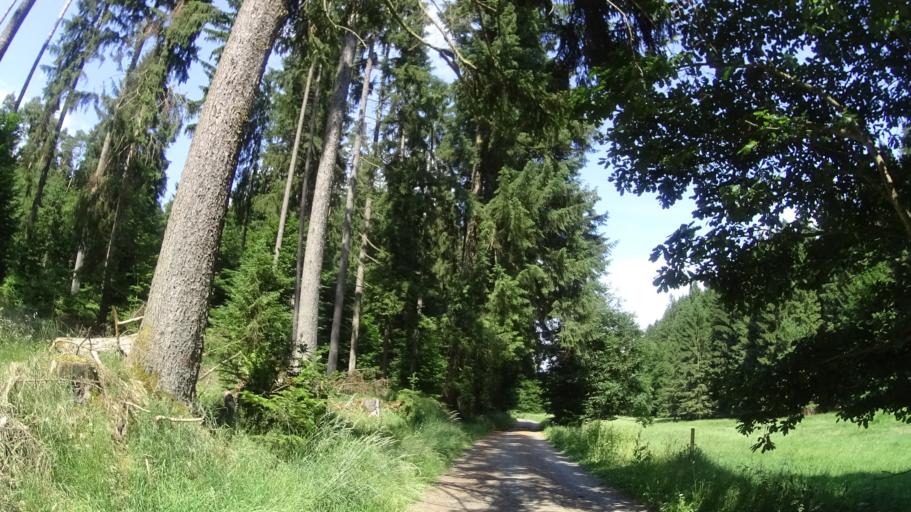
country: DE
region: Hesse
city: Rosenthal
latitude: 50.9668
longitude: 8.8305
